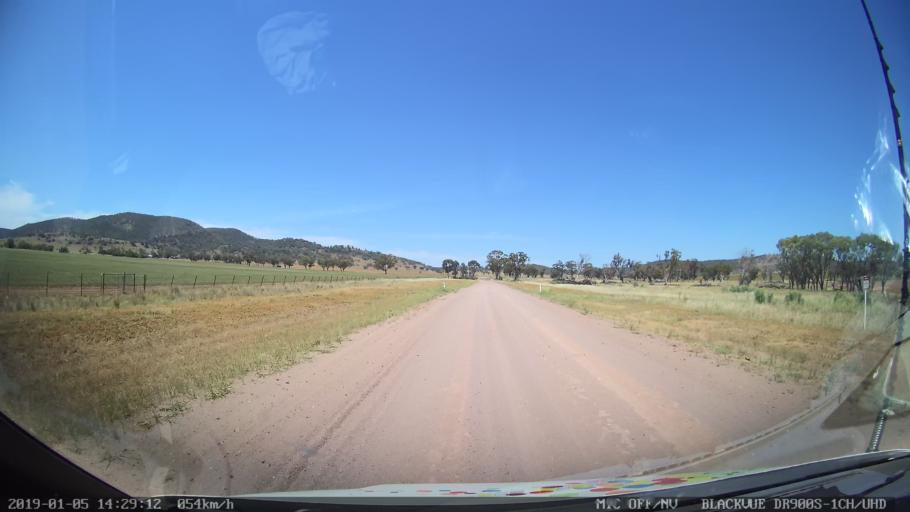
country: AU
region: New South Wales
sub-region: Tamworth Municipality
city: Phillip
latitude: -31.2298
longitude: 150.5796
